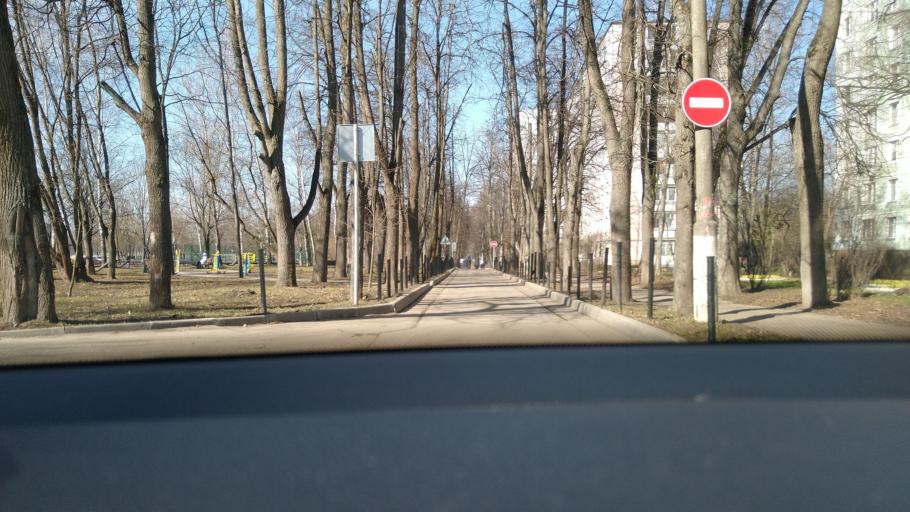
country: RU
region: Moscow
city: Rublevo
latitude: 55.7828
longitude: 37.3568
